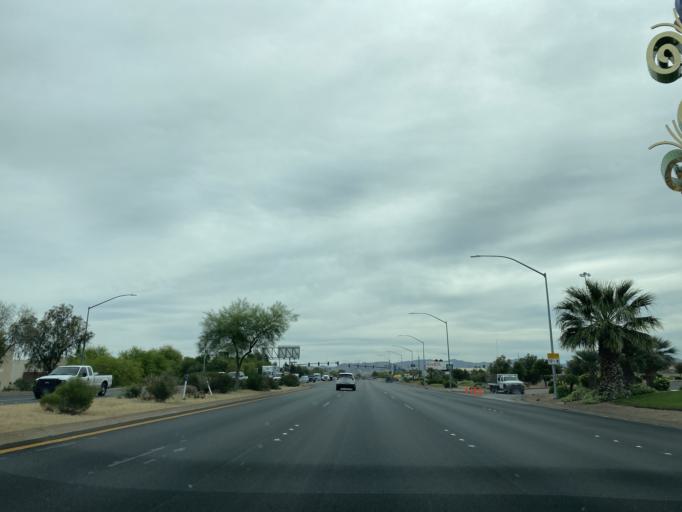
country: US
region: Nevada
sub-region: Clark County
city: Henderson
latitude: 36.0339
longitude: -115.0105
